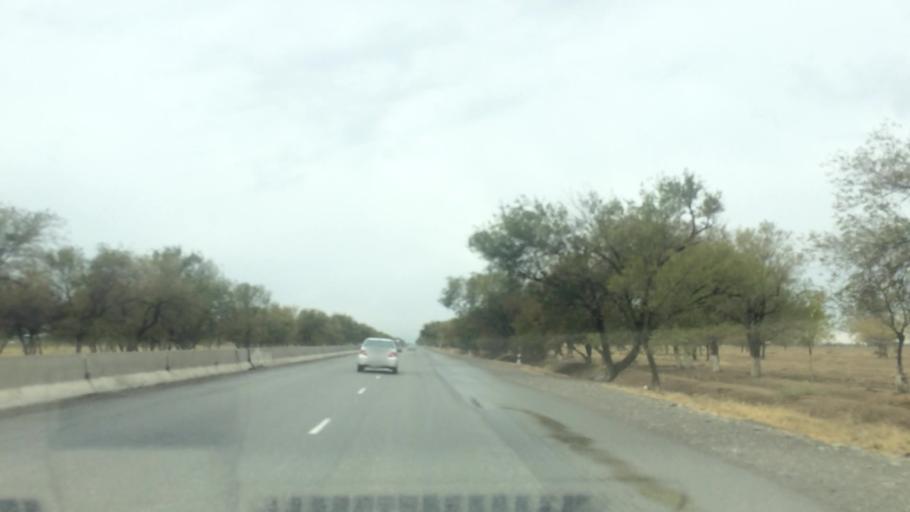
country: UZ
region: Samarqand
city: Bulung'ur
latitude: 39.8118
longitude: 67.3689
